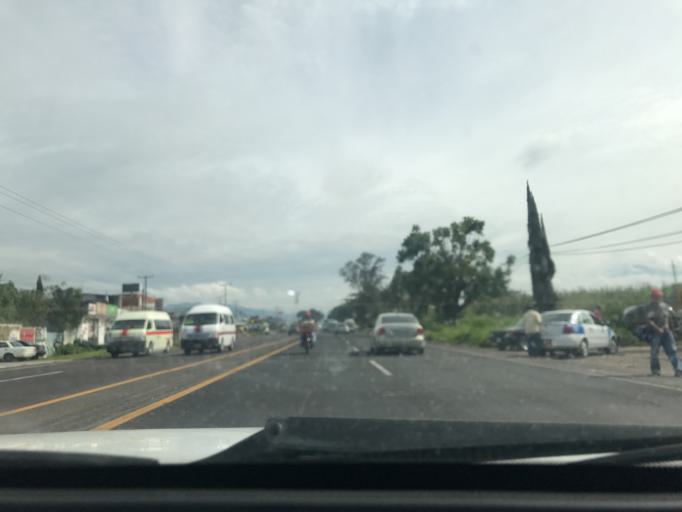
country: MX
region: Morelos
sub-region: Atlatlahucan
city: Colonia San Francisco
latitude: 18.8791
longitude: -98.9209
